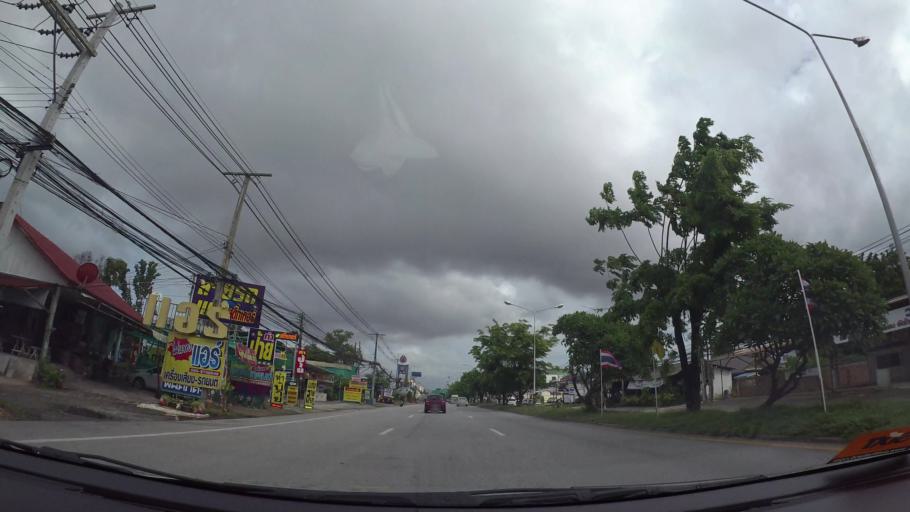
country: TH
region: Rayong
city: Rayong
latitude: 12.6875
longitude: 101.2117
